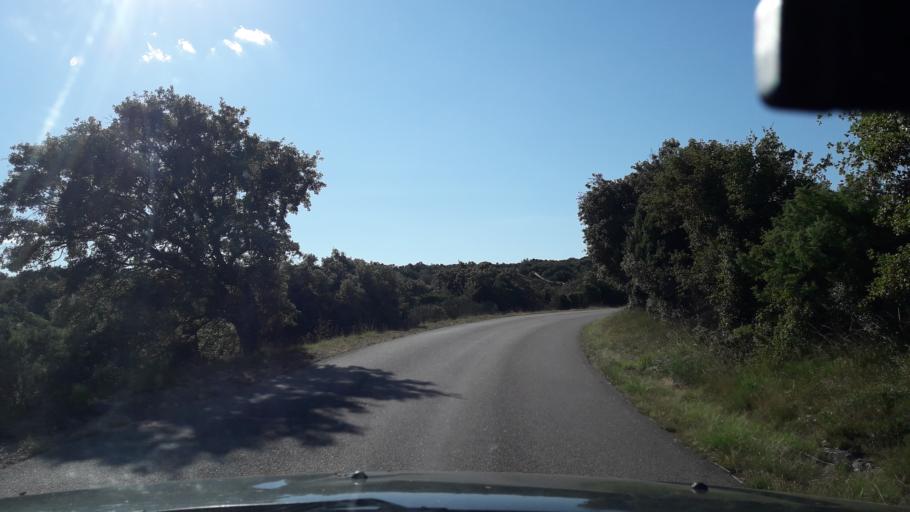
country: FR
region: Languedoc-Roussillon
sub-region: Departement du Gard
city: Saint-Julien-de-Peyrolas
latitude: 44.3659
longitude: 4.5235
